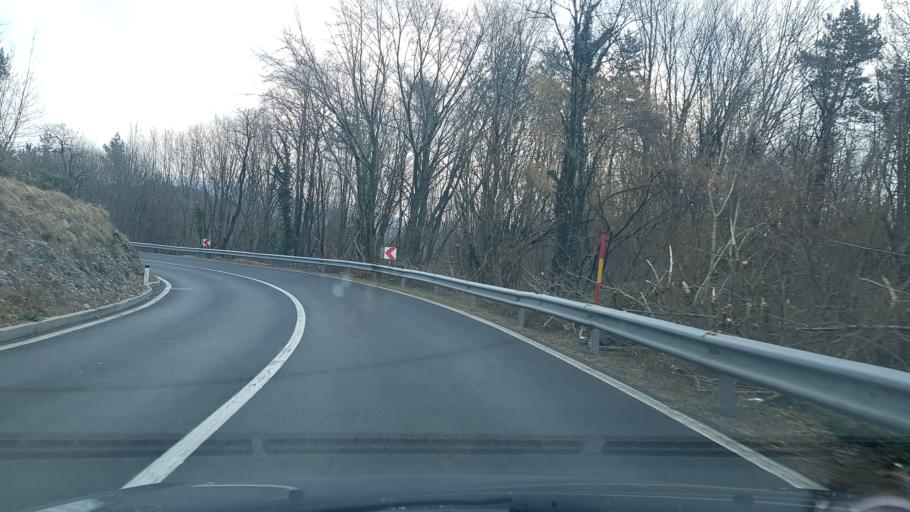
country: SI
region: Ilirska Bistrica
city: Ilirska Bistrica
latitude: 45.4913
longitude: 14.2049
